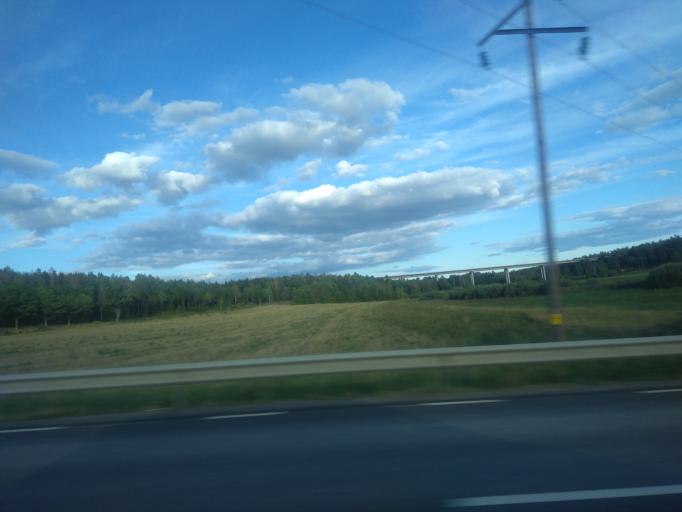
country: SE
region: OEstergoetland
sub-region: Norrkopings Kommun
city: Kimstad
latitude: 58.5135
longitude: 15.9819
